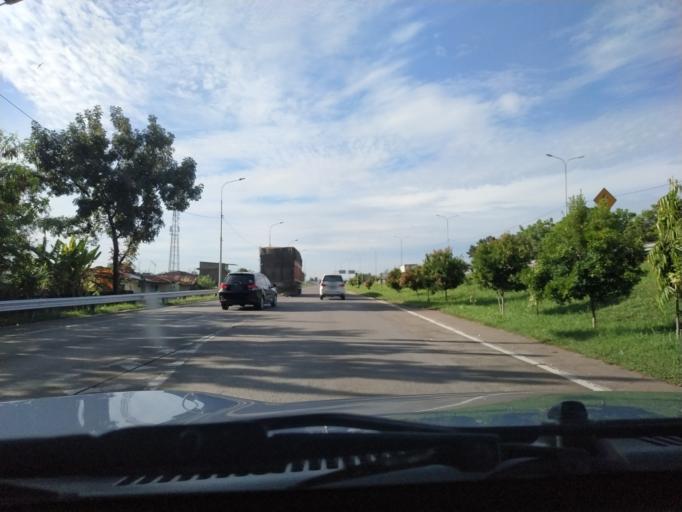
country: ID
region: North Sumatra
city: Medan
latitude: 3.5956
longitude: 98.7243
